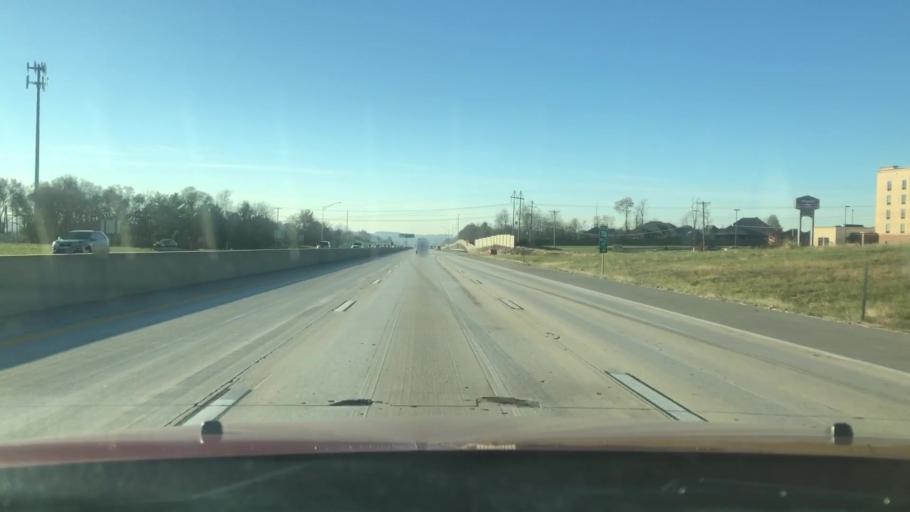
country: US
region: Missouri
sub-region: Greene County
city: Springfield
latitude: 37.1566
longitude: -93.2246
